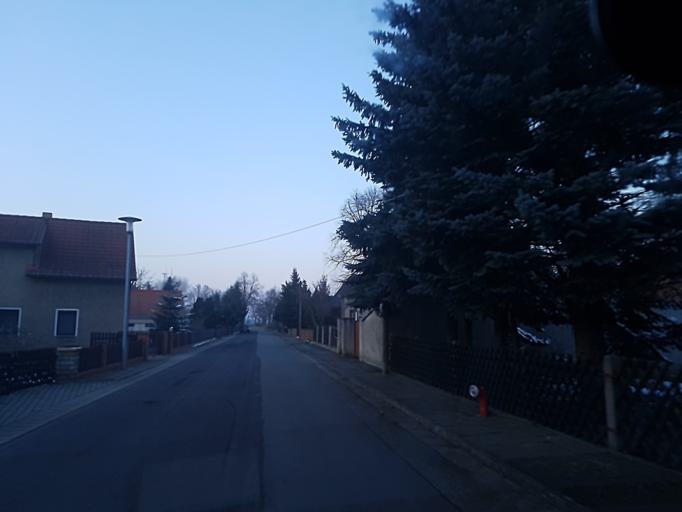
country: DE
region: Brandenburg
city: Bad Liebenwerda
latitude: 51.5140
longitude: 13.3456
